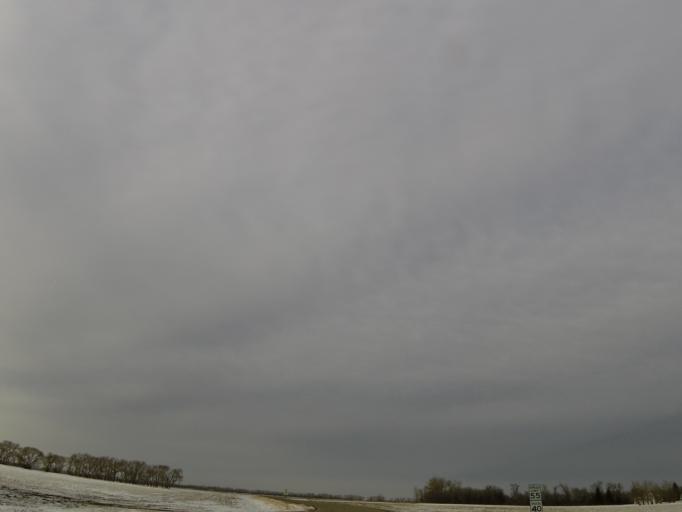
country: US
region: North Dakota
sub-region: Walsh County
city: Grafton
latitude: 48.4334
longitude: -97.2986
